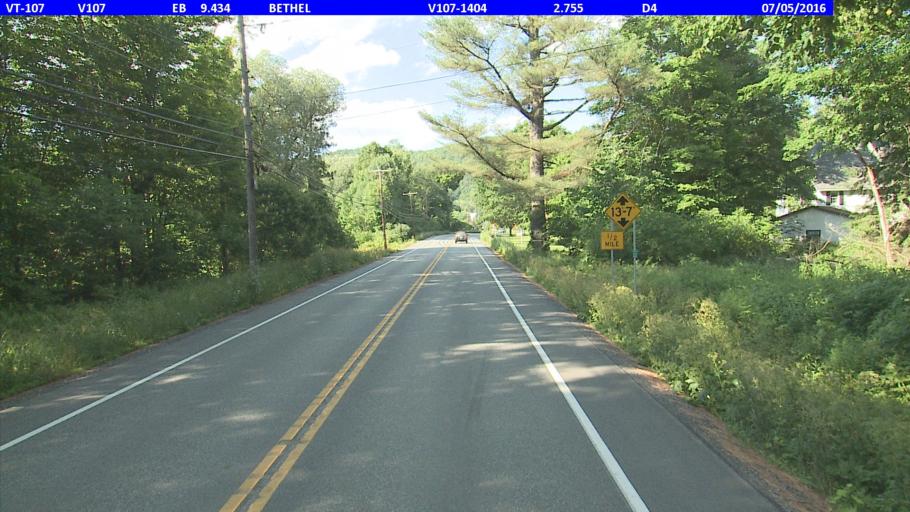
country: US
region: Vermont
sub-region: Orange County
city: Randolph
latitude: 43.8201
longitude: -72.6336
